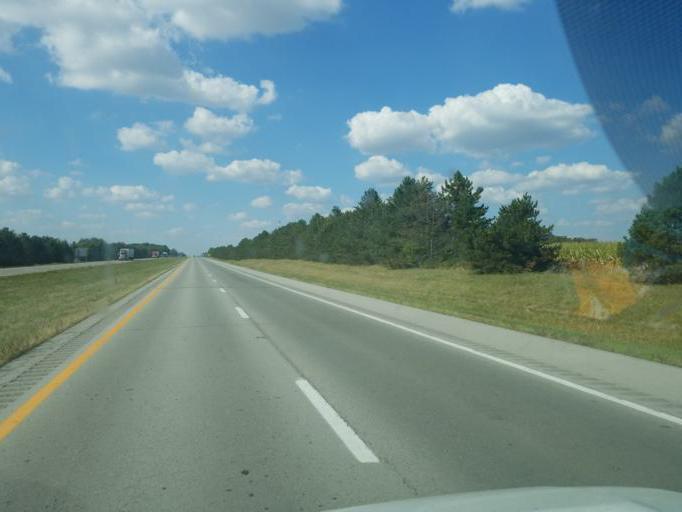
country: US
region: Ohio
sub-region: Wyandot County
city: Upper Sandusky
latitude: 40.8700
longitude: -83.3273
